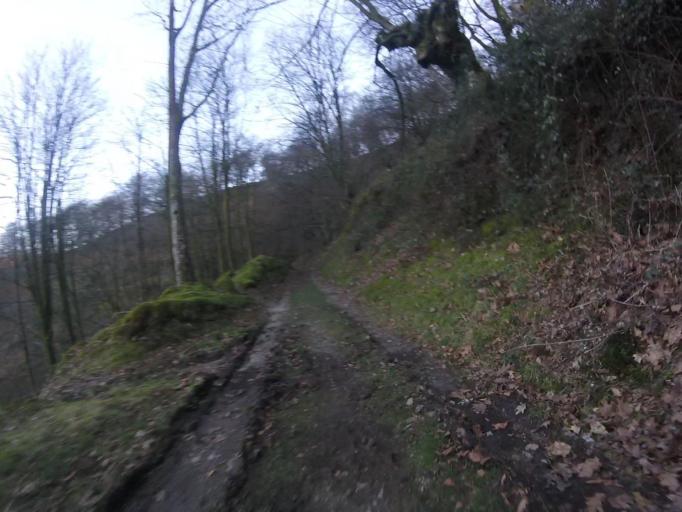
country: ES
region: Basque Country
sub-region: Provincia de Guipuzcoa
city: Irun
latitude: 43.2580
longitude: -1.8230
